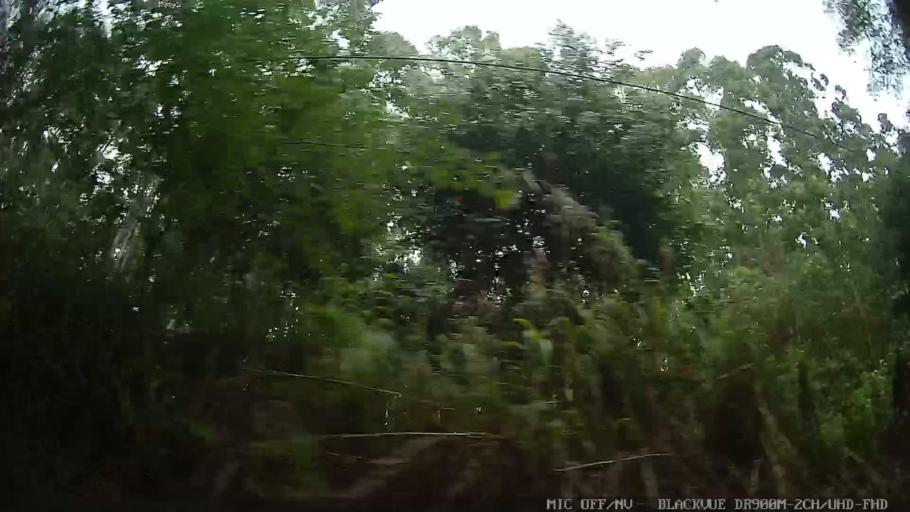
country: BR
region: Sao Paulo
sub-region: Itatiba
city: Itatiba
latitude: -23.0410
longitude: -46.8940
